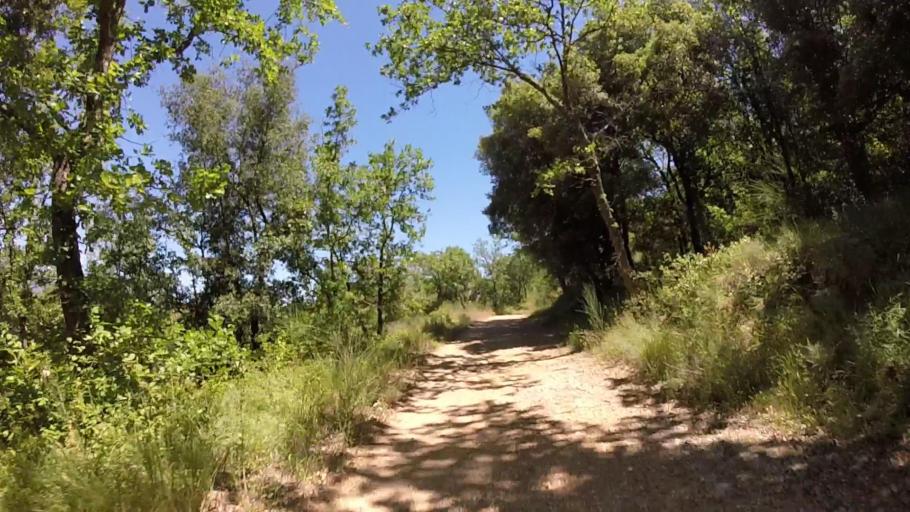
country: FR
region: Provence-Alpes-Cote d'Azur
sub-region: Departement des Alpes-Maritimes
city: Valbonne
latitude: 43.6351
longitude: 7.0284
